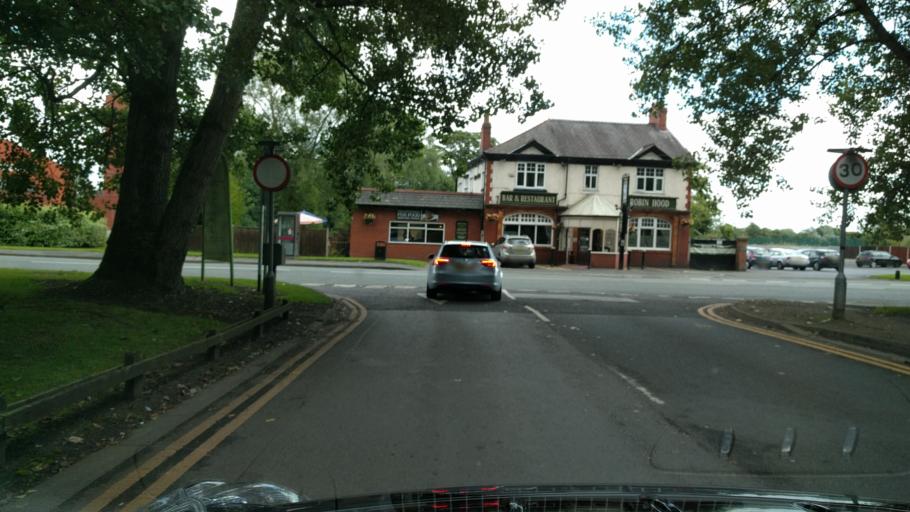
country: GB
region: England
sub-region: Borough of Wigan
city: Leigh
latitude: 53.4818
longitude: -2.5376
